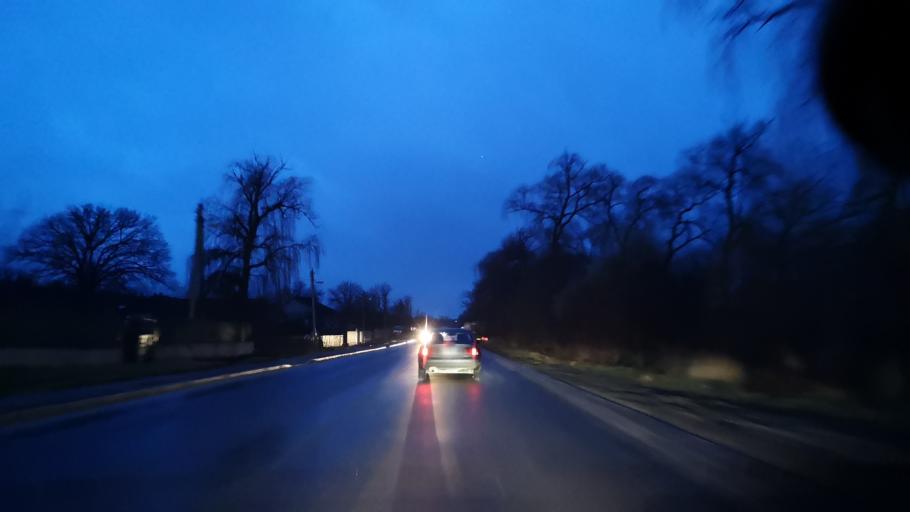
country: MD
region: Orhei
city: Orhei
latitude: 47.4255
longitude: 28.8040
